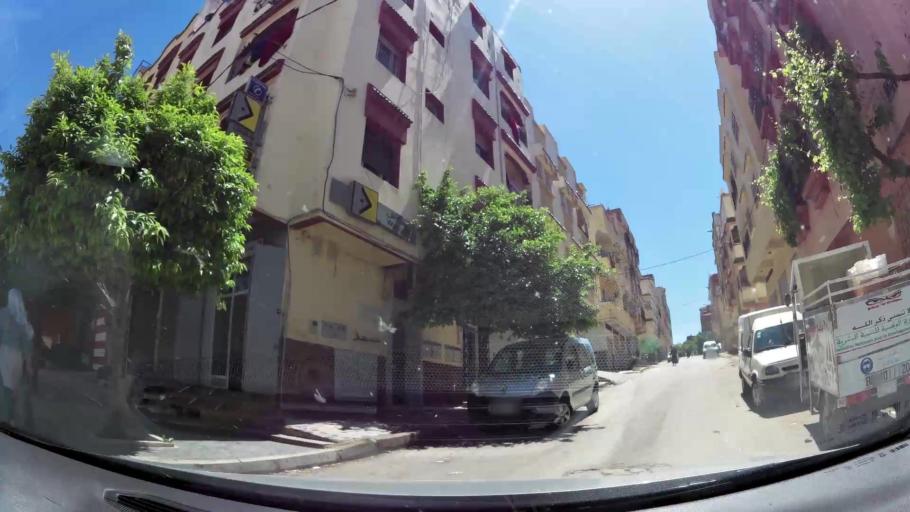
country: MA
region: Meknes-Tafilalet
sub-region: Meknes
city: Meknes
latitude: 33.8969
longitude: -5.5765
